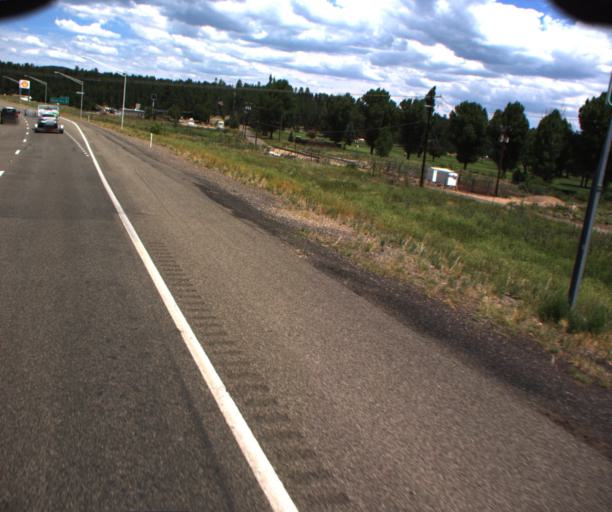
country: US
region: Arizona
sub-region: Coconino County
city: Sedona
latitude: 34.9371
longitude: -111.6495
